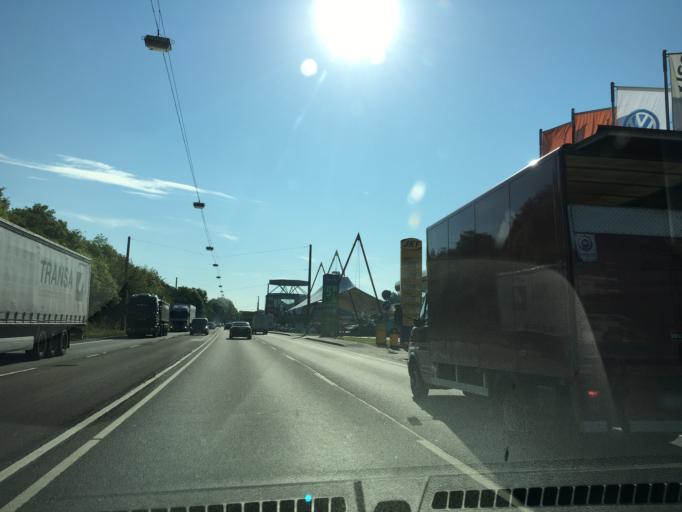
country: DE
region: North Rhine-Westphalia
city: Bad Oeynhausen
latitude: 52.2062
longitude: 8.7854
